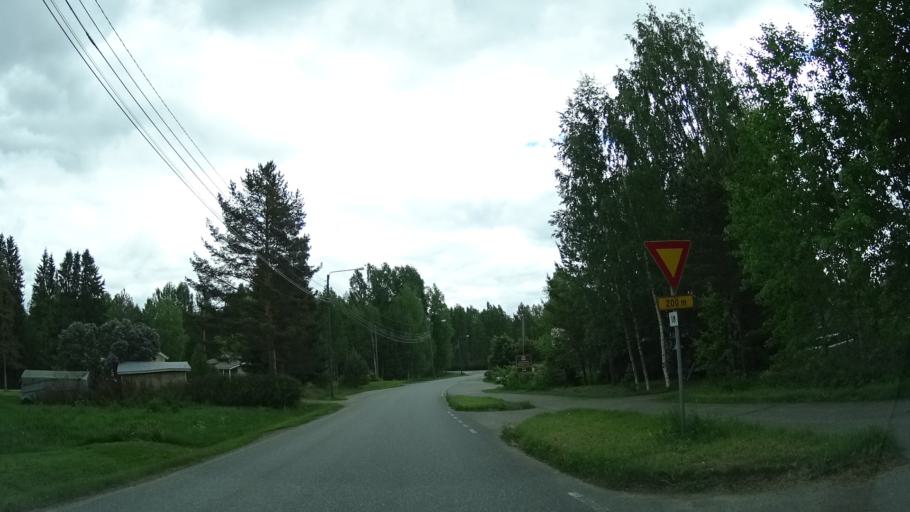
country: FI
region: Central Finland
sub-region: Jyvaeskylae
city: Toivakka
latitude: 61.9972
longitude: 25.9735
